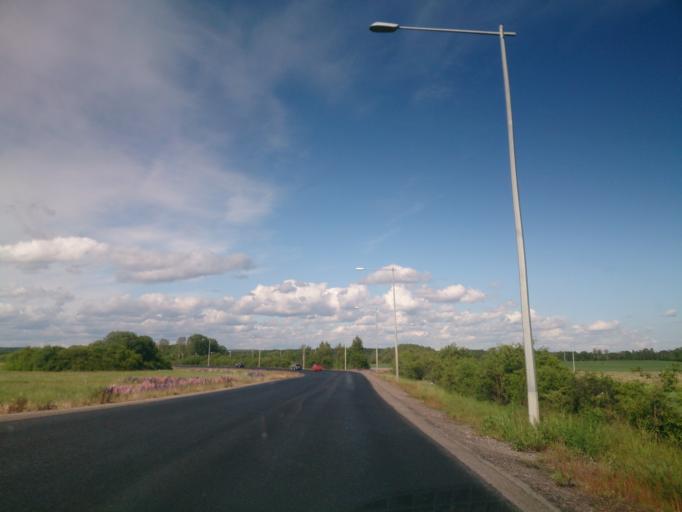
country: SE
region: OEstergoetland
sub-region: Norrkopings Kommun
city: Jursla
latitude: 58.6391
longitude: 16.1645
